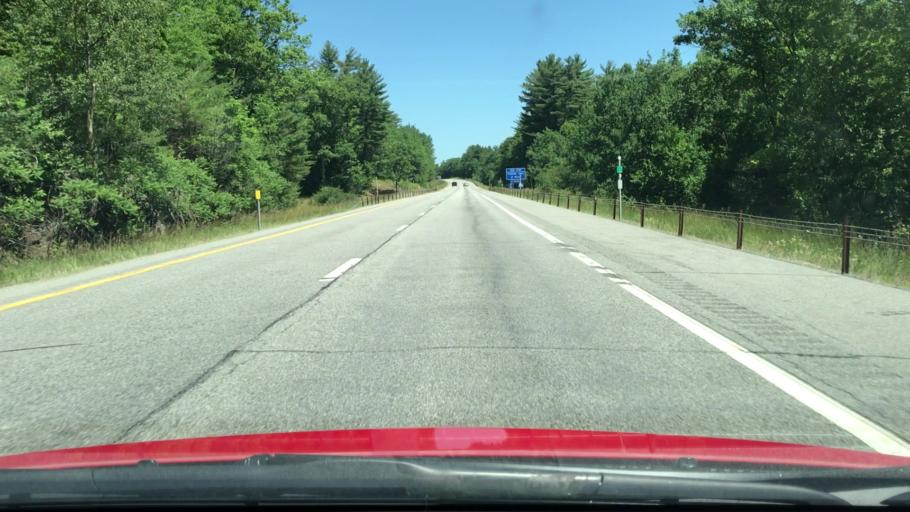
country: US
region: New York
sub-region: Essex County
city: Mineville
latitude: 44.1297
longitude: -73.5896
